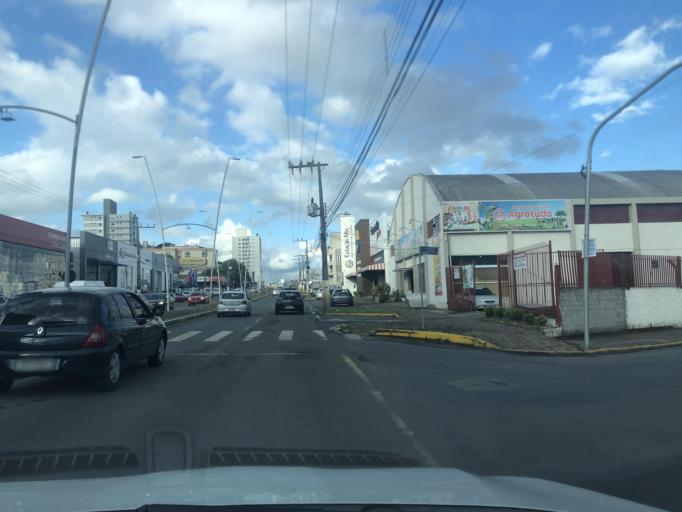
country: BR
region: Santa Catarina
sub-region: Lages
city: Lages
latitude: -27.8053
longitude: -50.3180
